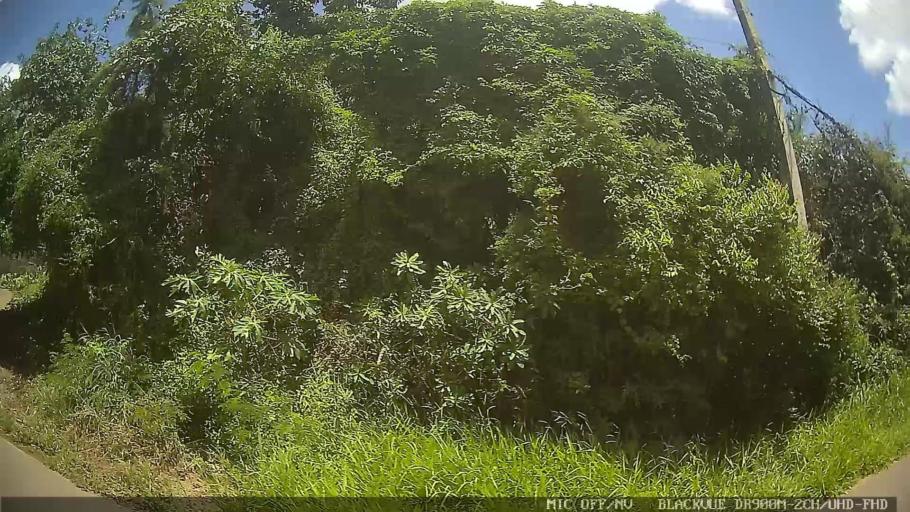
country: BR
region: Sao Paulo
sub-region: Braganca Paulista
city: Braganca Paulista
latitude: -22.9014
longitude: -46.5857
